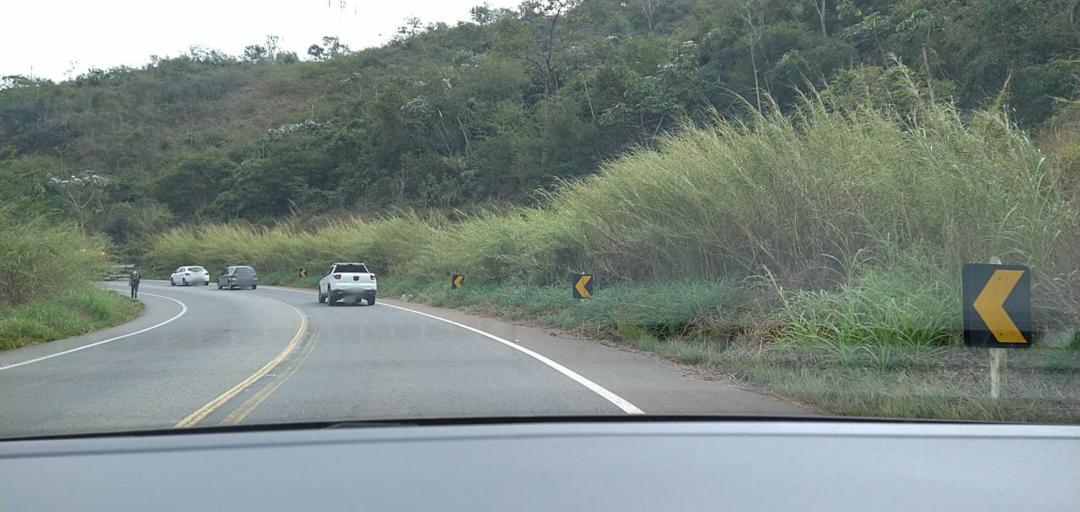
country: BR
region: Minas Gerais
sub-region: Ponte Nova
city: Ponte Nova
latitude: -20.5314
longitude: -42.8928
